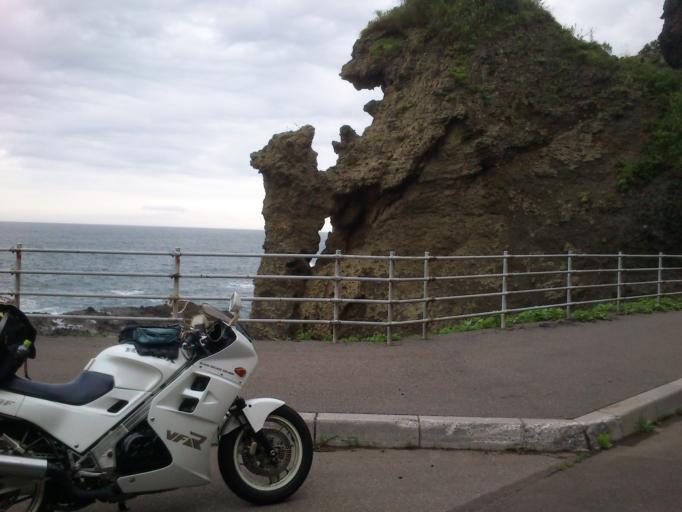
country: JP
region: Hokkaido
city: Kamiiso
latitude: 42.1524
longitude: 139.9129
